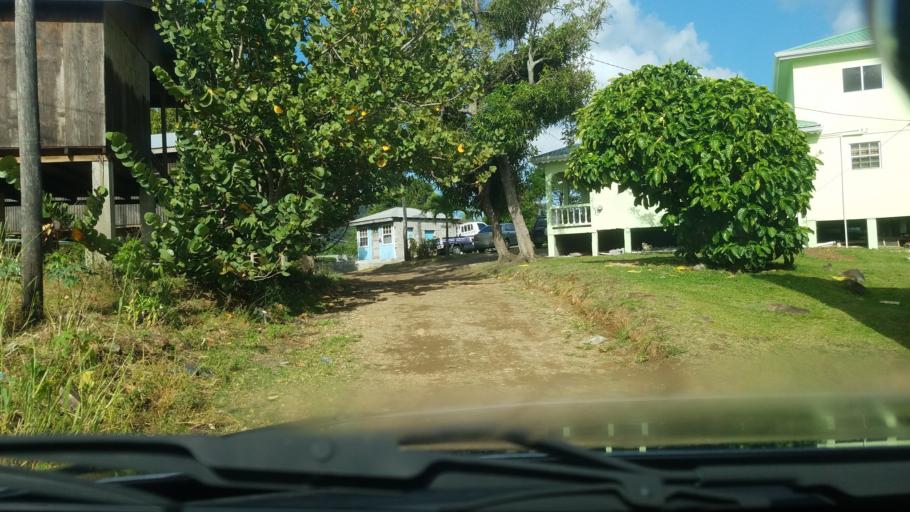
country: LC
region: Gros-Islet
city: Gros Islet
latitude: 14.0631
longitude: -60.9594
